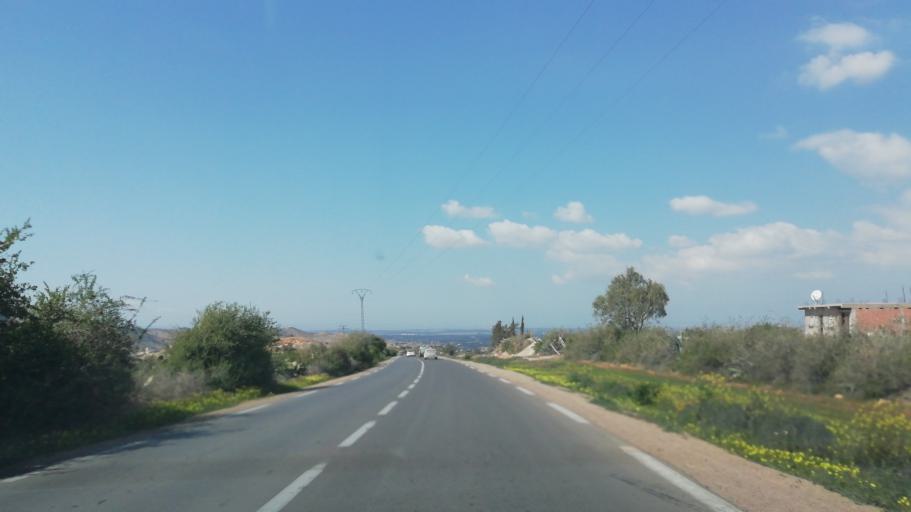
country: DZ
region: Mascara
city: Mascara
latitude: 35.5525
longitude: 0.0830
